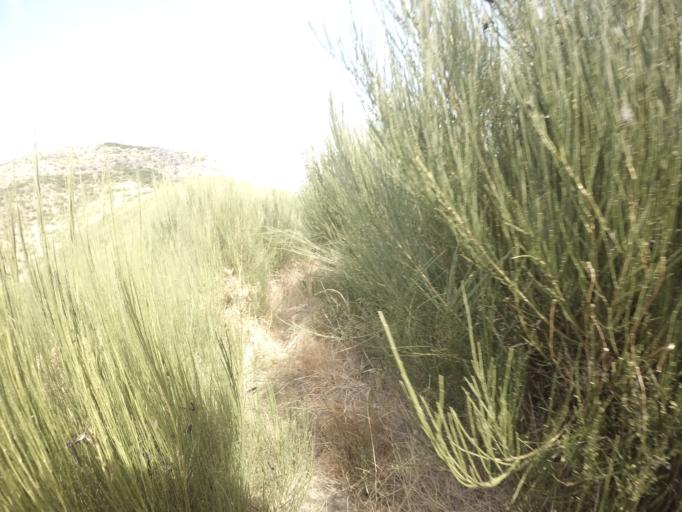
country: PT
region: Madeira
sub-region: Camara de Lobos
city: Curral das Freiras
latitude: 32.7157
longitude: -16.9982
